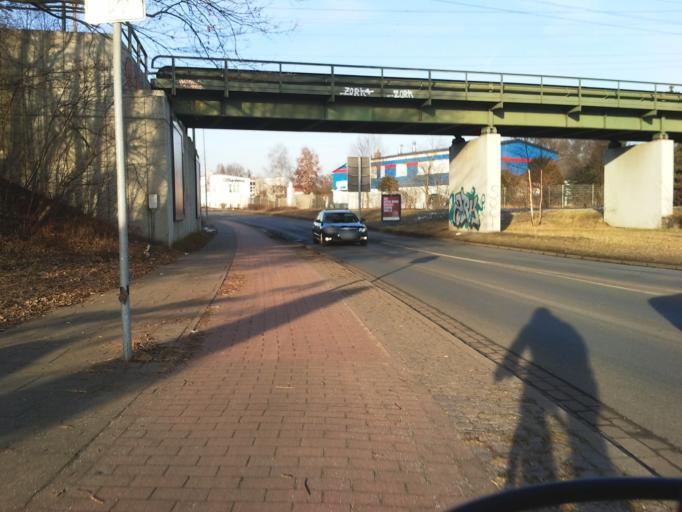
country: DE
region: Lower Saxony
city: Ritterhude
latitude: 53.1403
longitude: 8.7138
